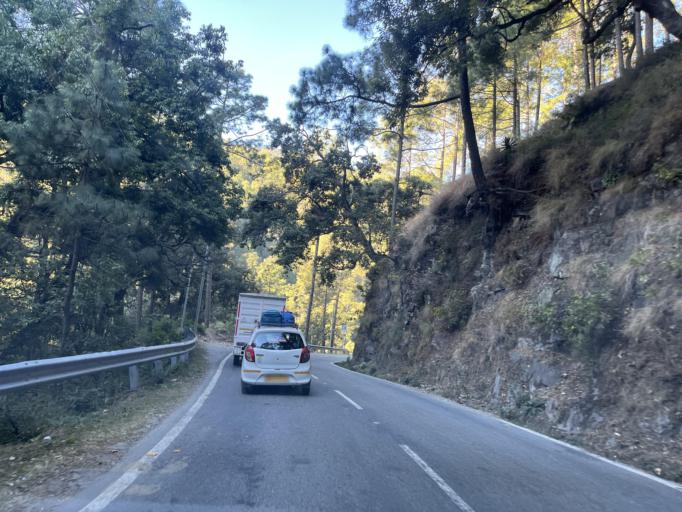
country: IN
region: Uttarakhand
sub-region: Naini Tal
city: Bhowali
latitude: 29.3980
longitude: 79.5114
